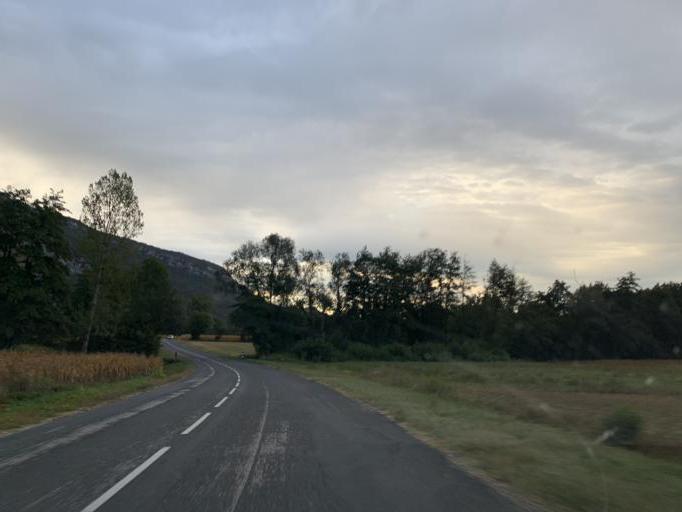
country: FR
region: Rhone-Alpes
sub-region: Departement de l'Isere
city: Les Avenieres
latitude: 45.7007
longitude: 5.5809
